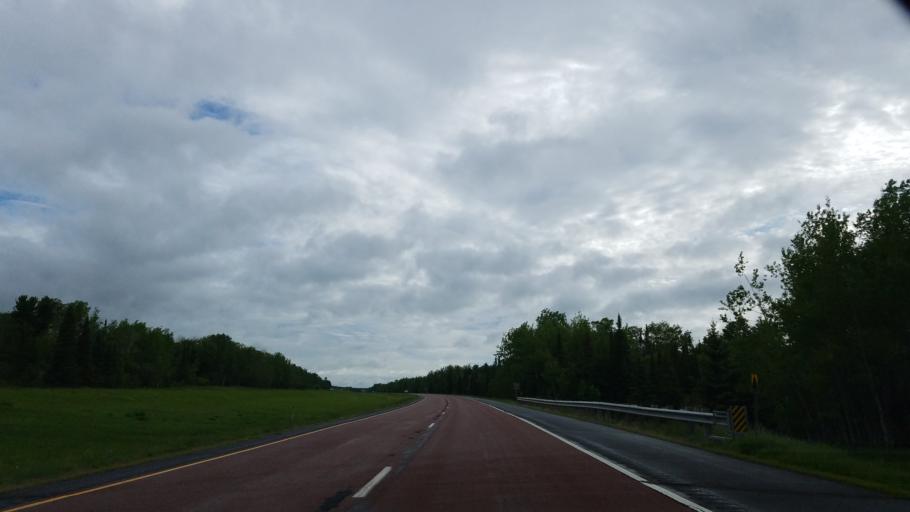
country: US
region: Minnesota
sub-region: Saint Louis County
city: Arnold
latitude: 46.8943
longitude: -91.9101
